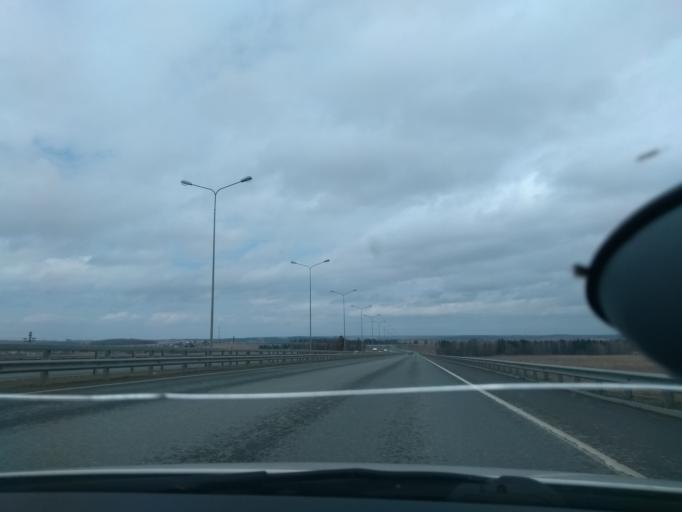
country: RU
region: Perm
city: Zvezdnyy
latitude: 57.7723
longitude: 56.3375
